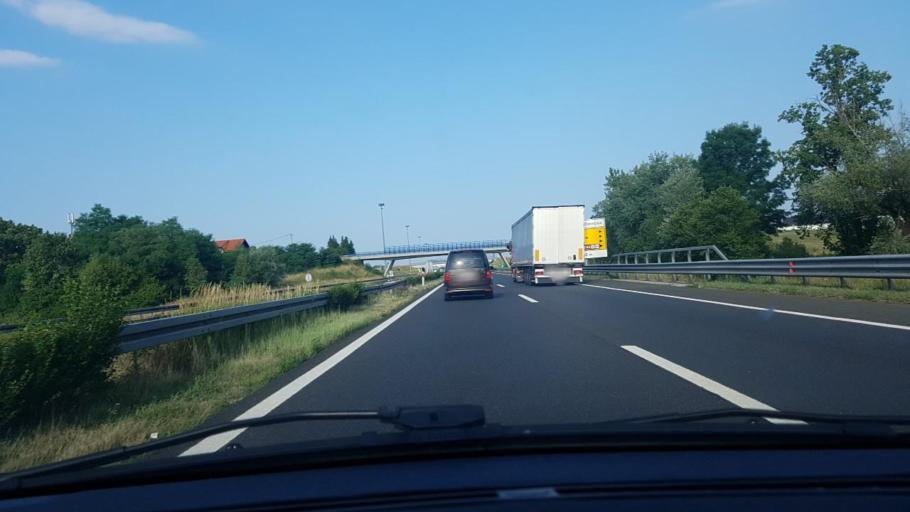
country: HR
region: Grad Zagreb
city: Horvati
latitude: 45.6763
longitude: 15.7619
